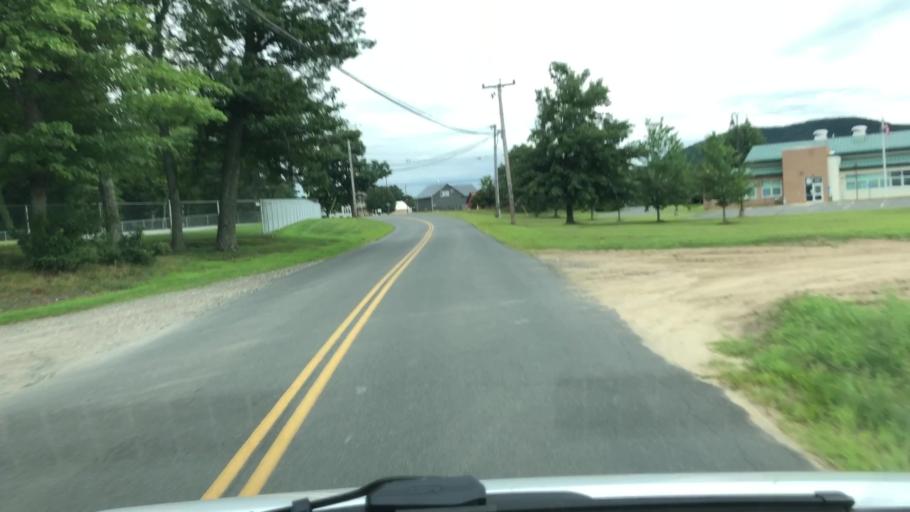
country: US
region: Massachusetts
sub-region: Franklin County
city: South Deerfield
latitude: 42.4606
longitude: -72.6087
